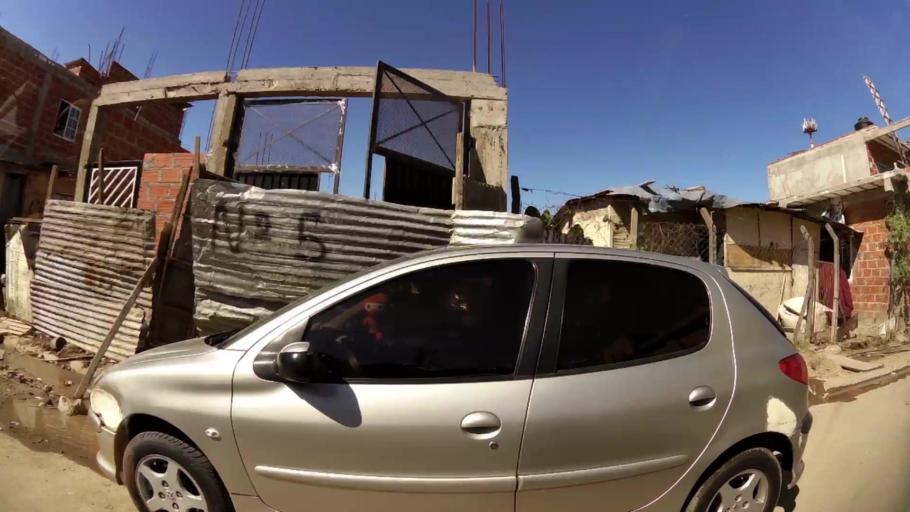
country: AR
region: Buenos Aires
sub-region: Partido de General San Martin
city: General San Martin
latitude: -34.5330
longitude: -58.5786
